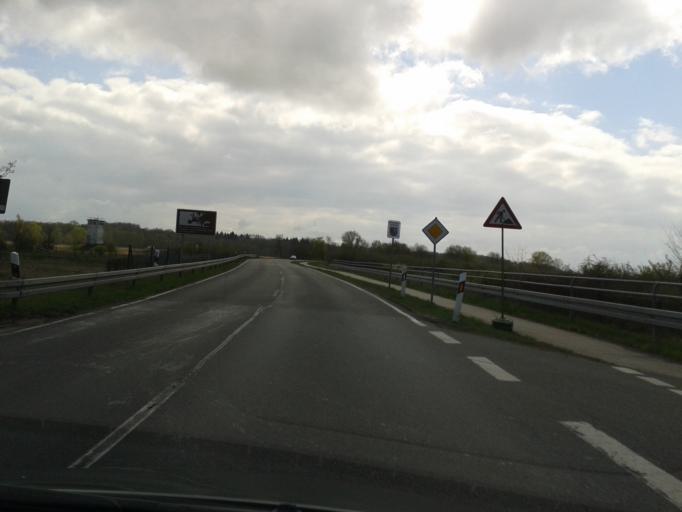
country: DE
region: Lower Saxony
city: Lubbow
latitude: 52.9022
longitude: 11.1789
